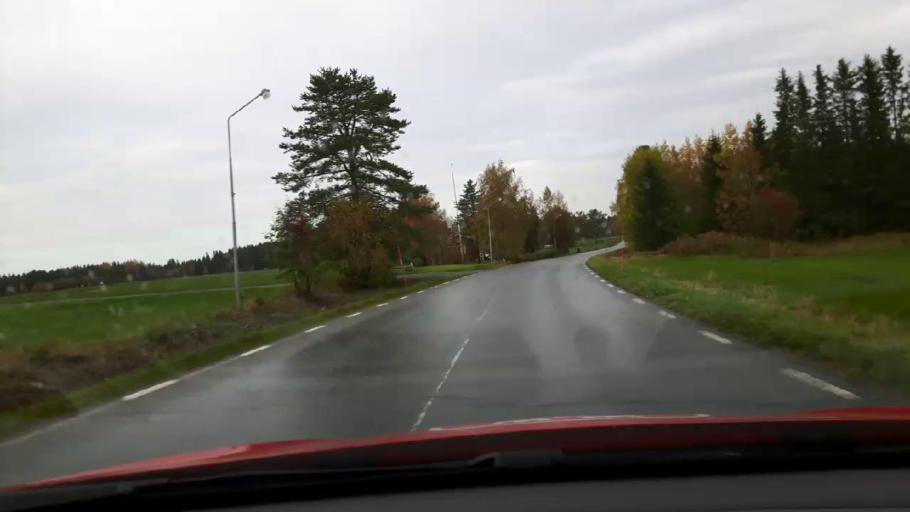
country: SE
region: Jaemtland
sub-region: Bergs Kommun
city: Hoverberg
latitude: 63.0217
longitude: 14.3428
